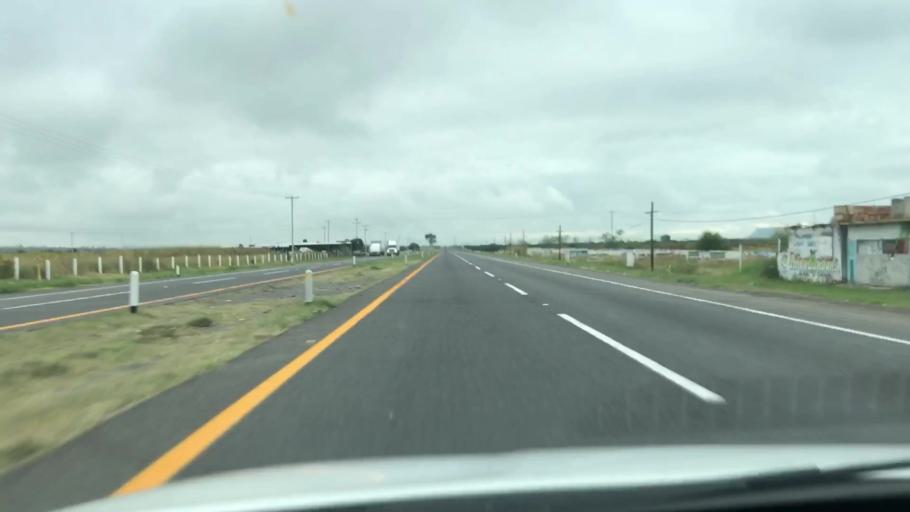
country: MX
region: Jalisco
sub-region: Lagos de Moreno
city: Cristeros [Fraccionamiento]
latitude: 21.3014
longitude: -102.1131
